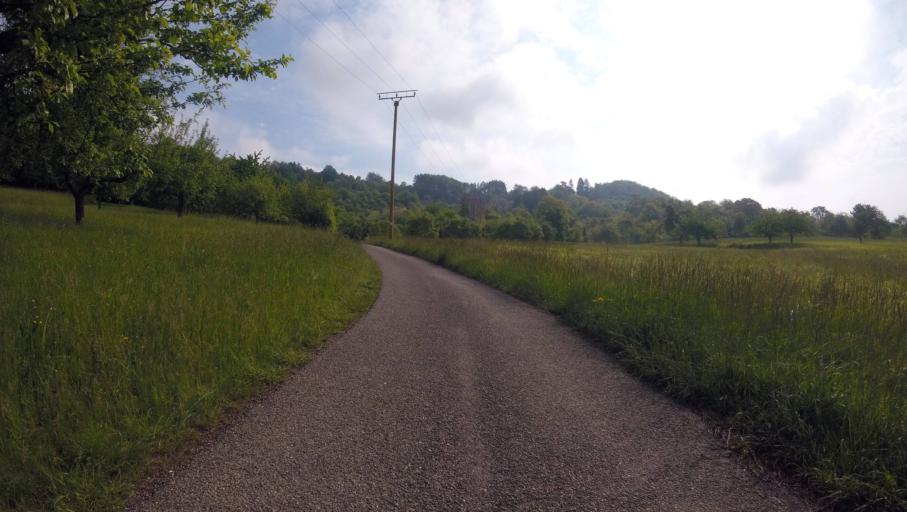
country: DE
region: Baden-Wuerttemberg
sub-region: Regierungsbezirk Stuttgart
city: Althutte
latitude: 48.9317
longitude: 9.5312
